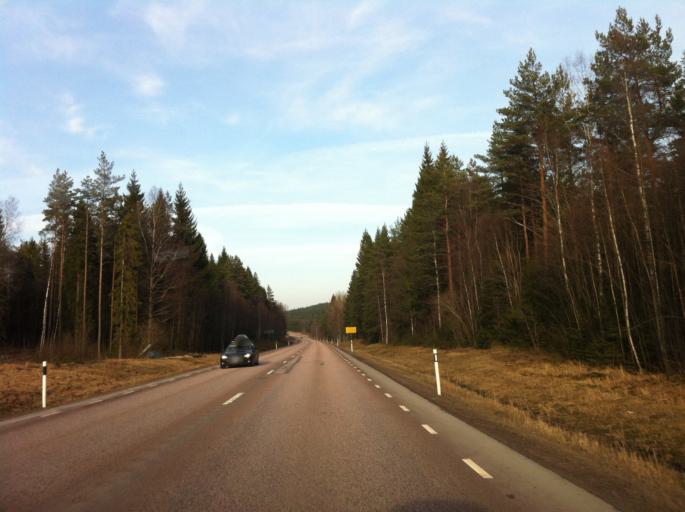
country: SE
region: Vaermland
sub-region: Kristinehamns Kommun
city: Kristinehamn
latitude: 59.3640
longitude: 14.1575
